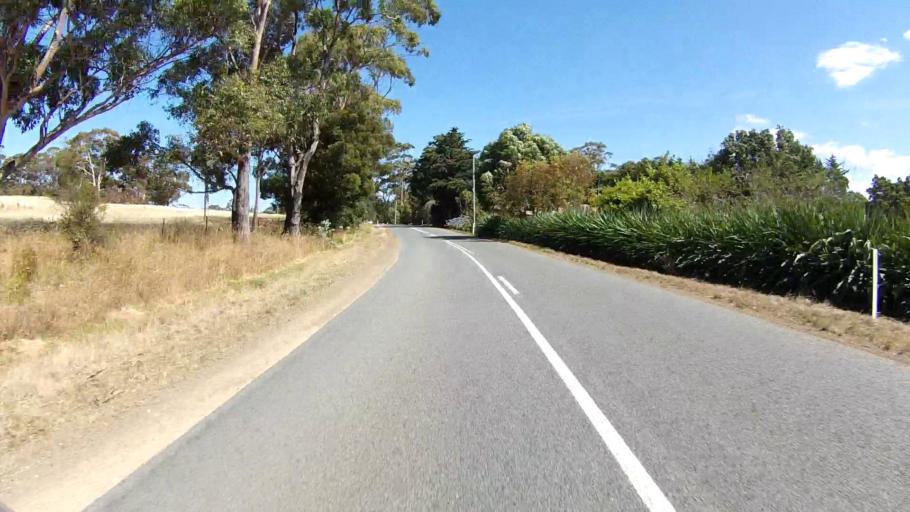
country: AU
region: Tasmania
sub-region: Sorell
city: Sorell
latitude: -42.3073
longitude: 147.9636
